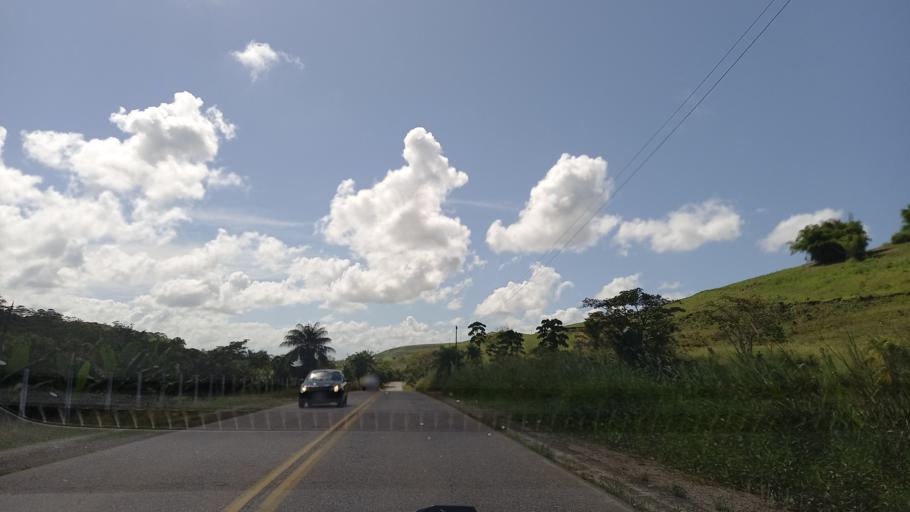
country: BR
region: Pernambuco
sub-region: Barreiros
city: Barreiros
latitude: -8.7628
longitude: -35.1695
